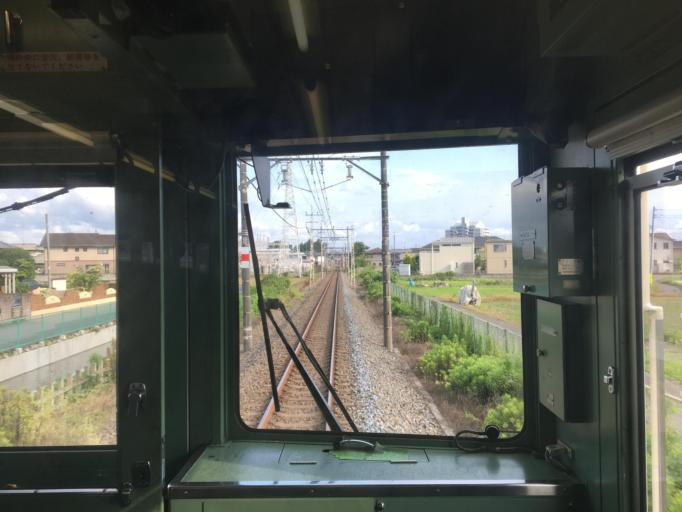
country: JP
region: Tochigi
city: Ashikaga
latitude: 36.3115
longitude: 139.4562
